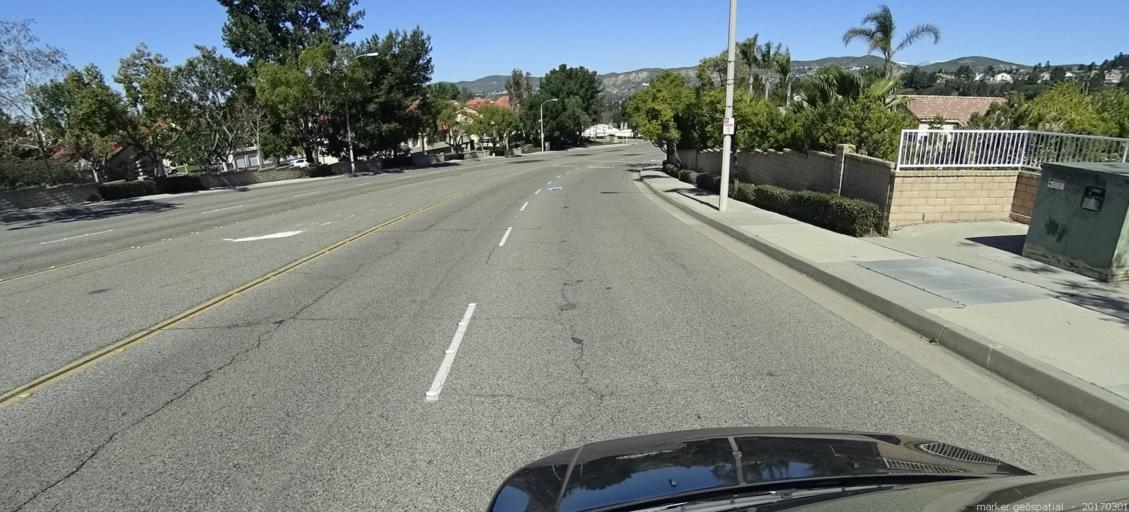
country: US
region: California
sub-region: Orange County
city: Yorba Linda
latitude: 33.8588
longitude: -117.7371
